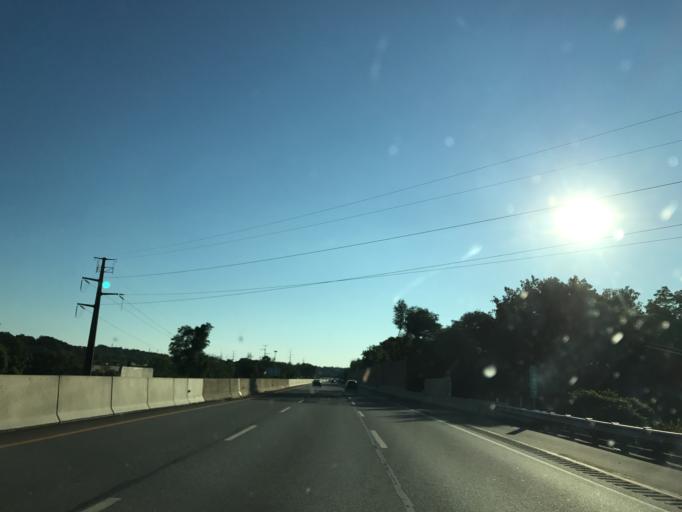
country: US
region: Pennsylvania
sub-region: Montgomery County
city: Hatboro
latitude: 40.1634
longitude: -75.1047
